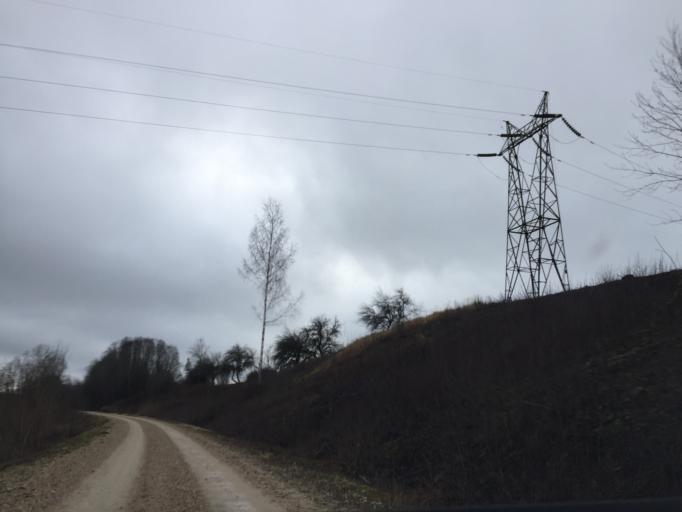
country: LV
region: Broceni
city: Broceni
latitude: 56.6879
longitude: 22.5578
